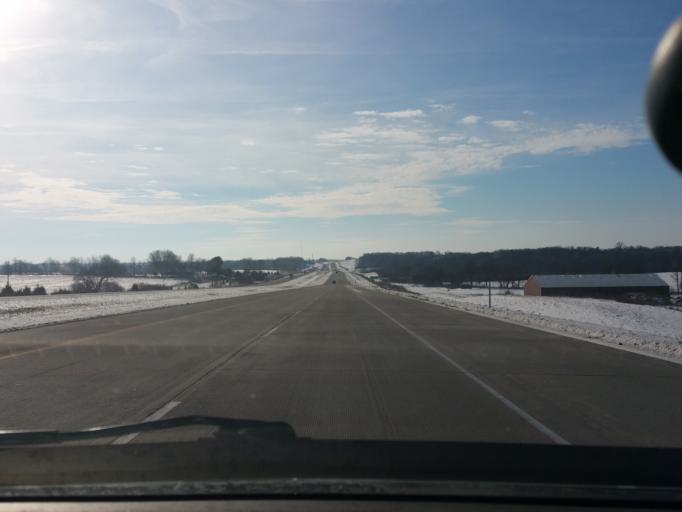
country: US
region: Iowa
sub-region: Warren County
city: Norwalk
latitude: 41.4708
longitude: -93.7804
